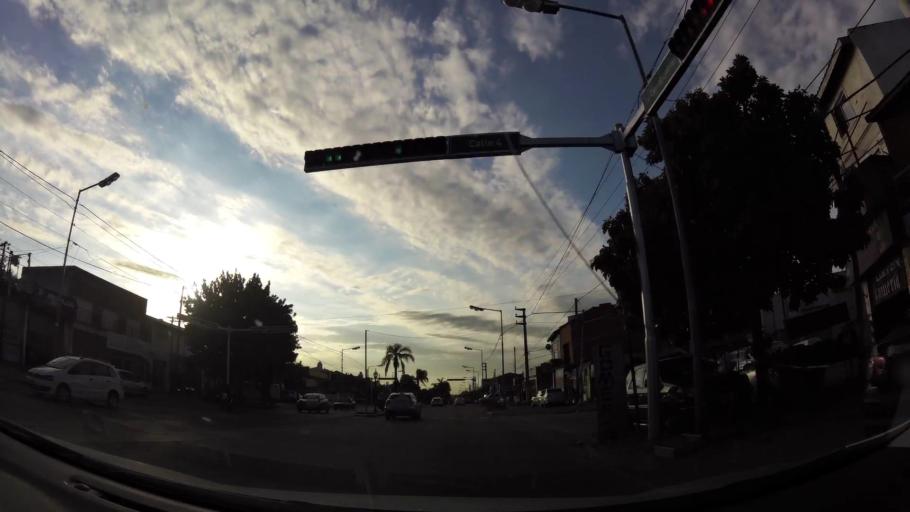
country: AR
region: Buenos Aires
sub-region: Partido de Tigre
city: Tigre
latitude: -34.4527
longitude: -58.6517
